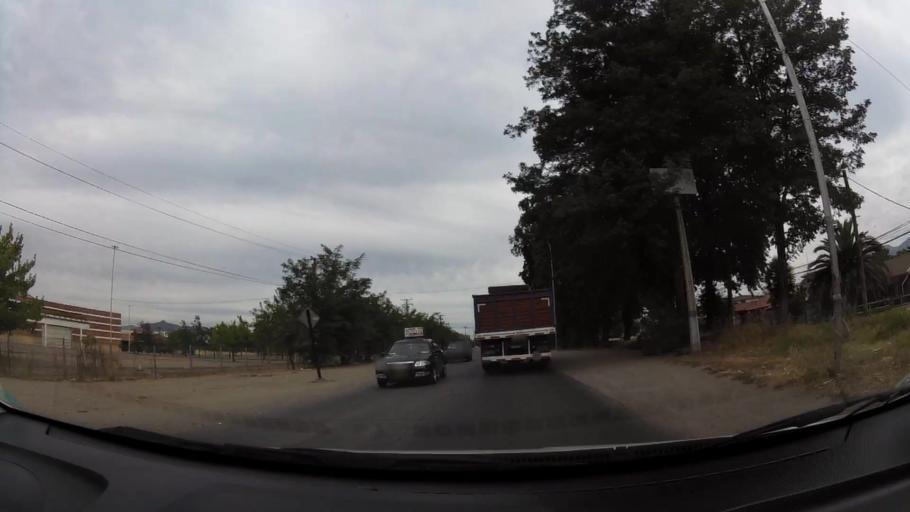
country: CL
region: O'Higgins
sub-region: Provincia de Cachapoal
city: Rancagua
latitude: -34.1351
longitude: -70.7314
